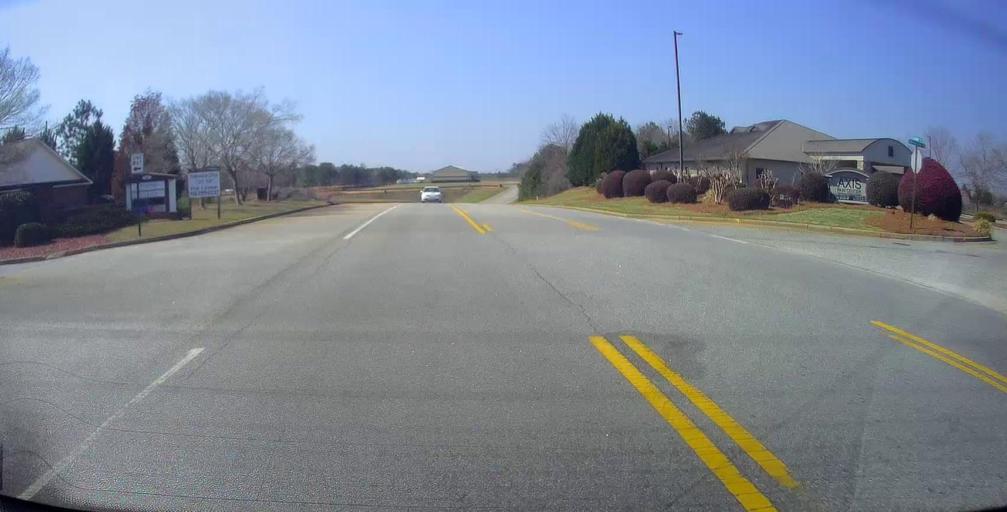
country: US
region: Georgia
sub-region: Houston County
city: Centerville
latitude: 32.6126
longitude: -83.6993
